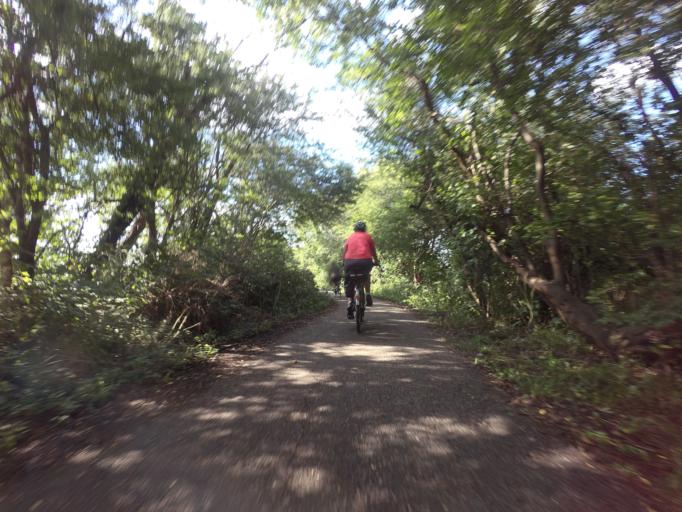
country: GB
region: England
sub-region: East Sussex
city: Hailsham
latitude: 50.8737
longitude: 0.2509
